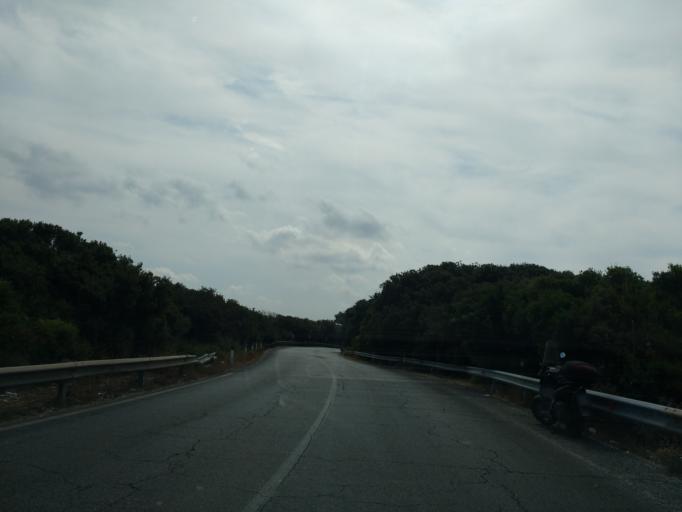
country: IT
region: Latium
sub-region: Citta metropolitana di Roma Capitale
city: Torvaianica
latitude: 41.6681
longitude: 12.4015
